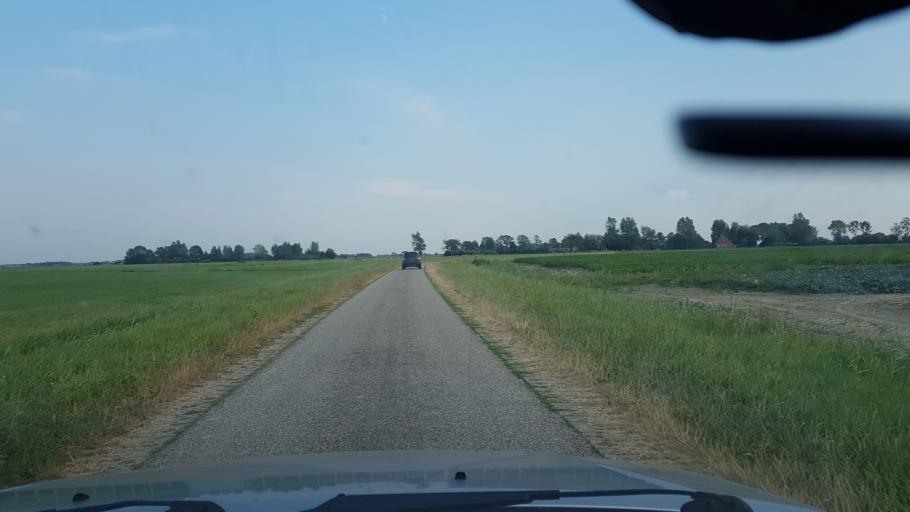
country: NL
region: Friesland
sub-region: Gemeente Ferwerderadiel
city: Burdaard
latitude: 53.3353
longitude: 5.8682
